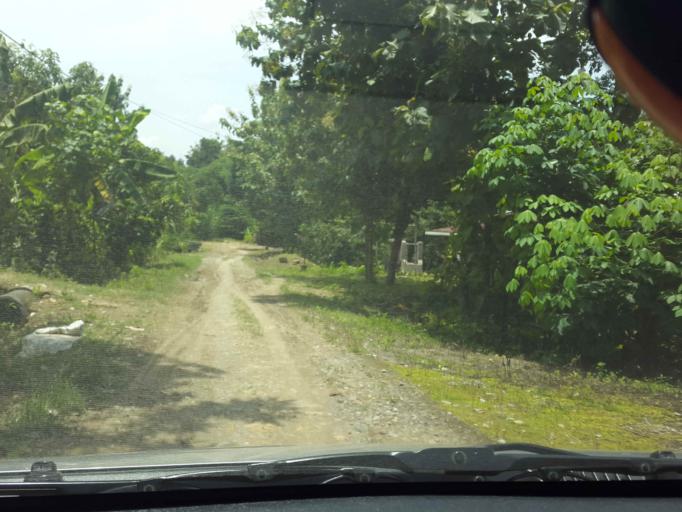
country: ID
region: Central Java
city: Sragen
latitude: -7.2980
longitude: 110.9763
